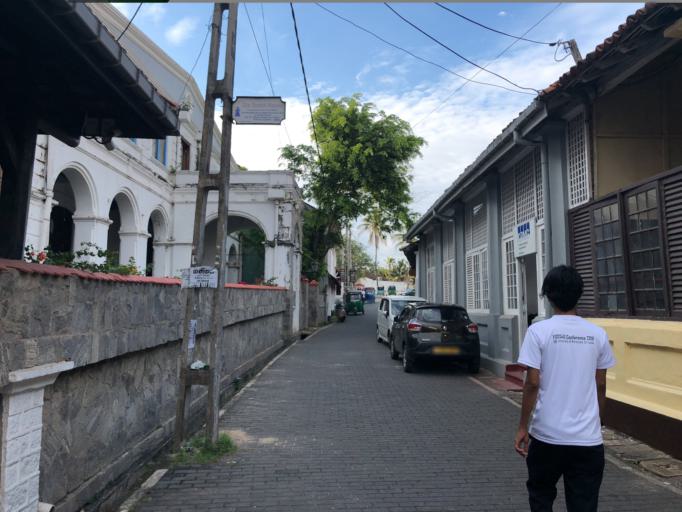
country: LK
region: Southern
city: Galle
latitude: 6.0281
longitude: 80.2158
